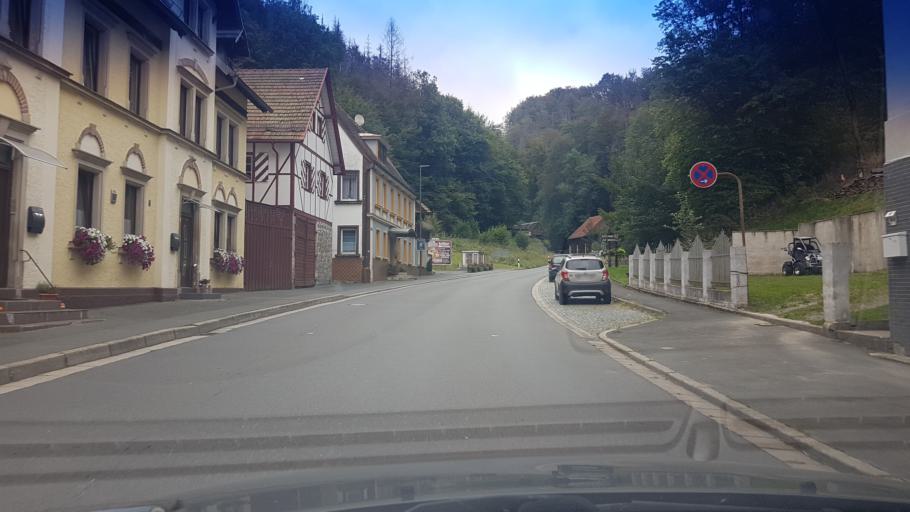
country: DE
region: Bavaria
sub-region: Upper Franconia
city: Bad Berneck im Fichtelgebirge
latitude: 50.0524
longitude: 11.6736
